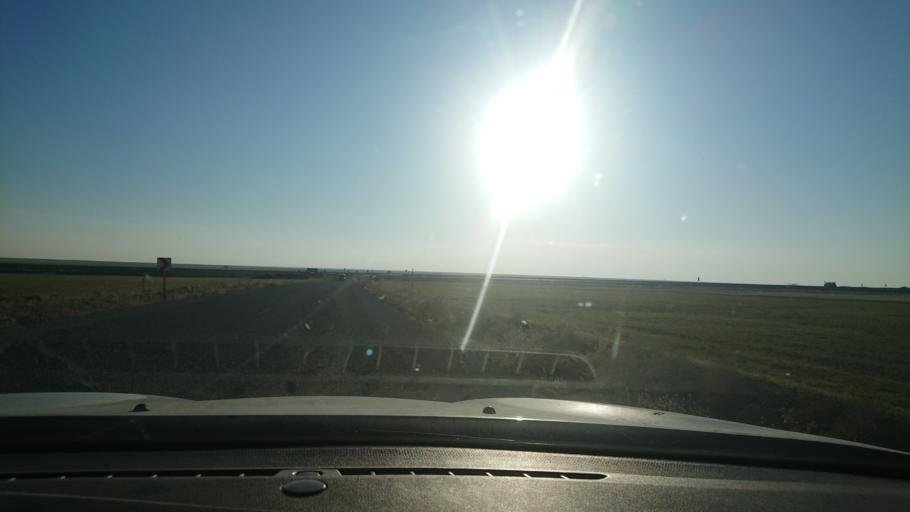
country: TR
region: Aksaray
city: Acipinar
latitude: 38.6641
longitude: 33.7174
